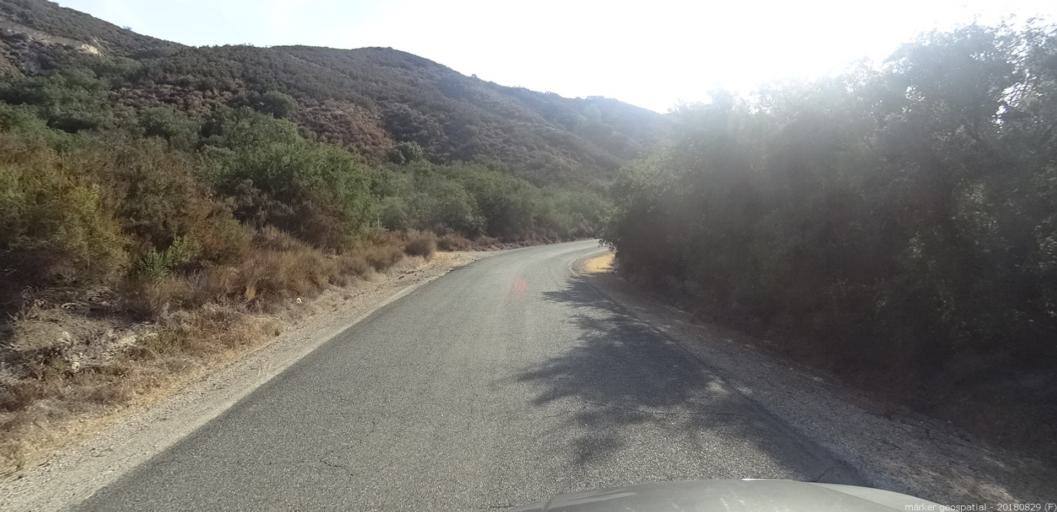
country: US
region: California
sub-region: Monterey County
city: King City
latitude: 36.0284
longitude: -121.0713
